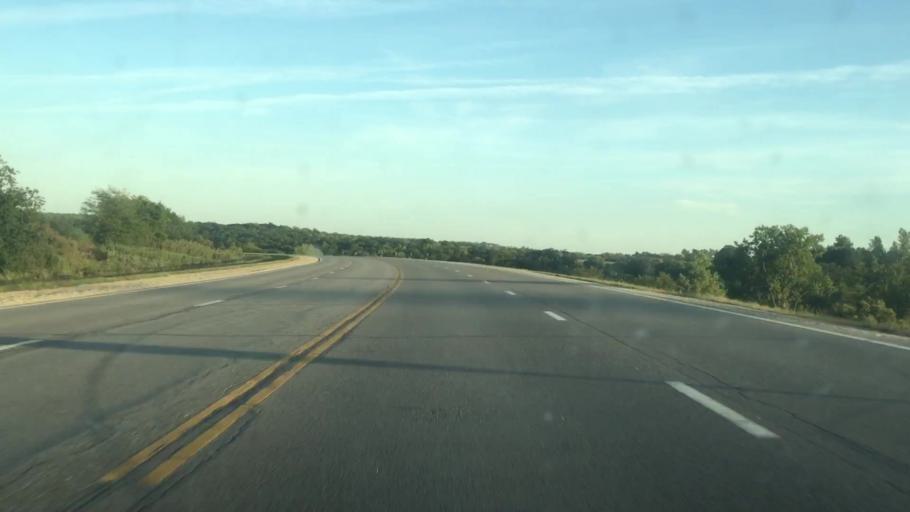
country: US
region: Kansas
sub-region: Atchison County
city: Atchison
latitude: 39.4881
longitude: -95.1298
